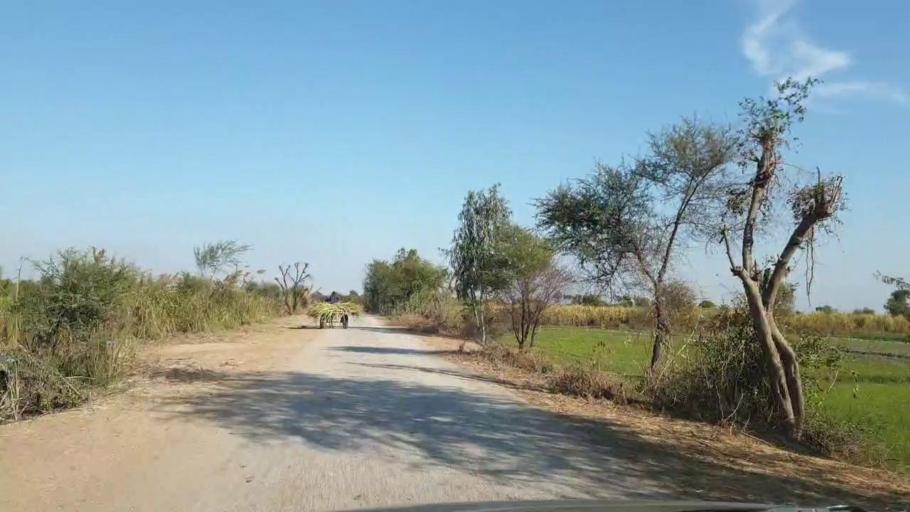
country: PK
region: Sindh
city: Khadro
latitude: 26.1895
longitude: 68.7507
